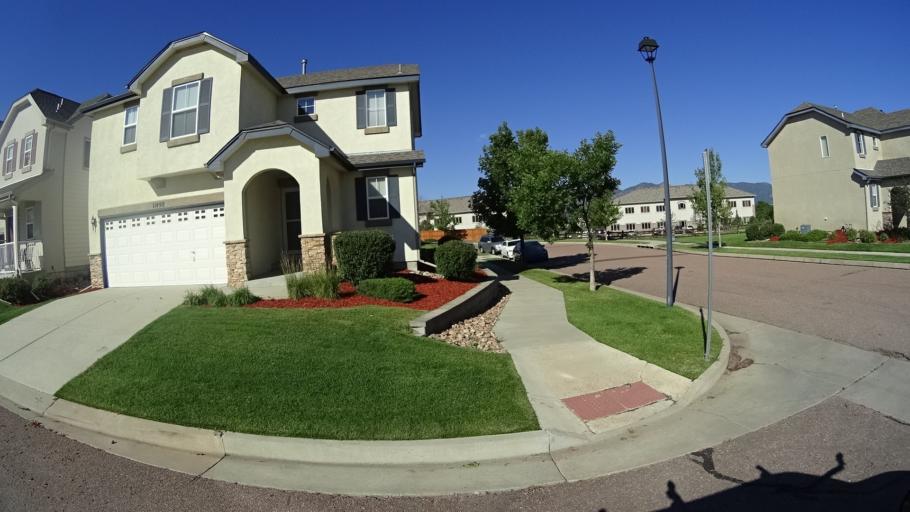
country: US
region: Colorado
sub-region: El Paso County
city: Gleneagle
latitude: 38.9981
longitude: -104.7960
